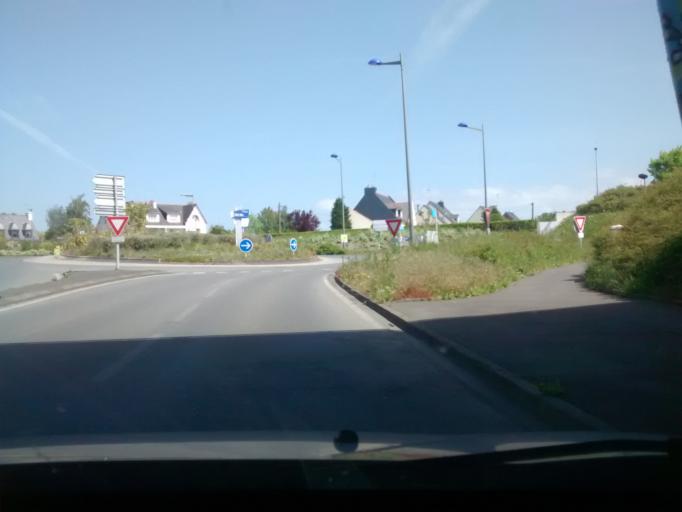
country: FR
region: Brittany
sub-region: Departement des Cotes-d'Armor
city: Langueux
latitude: 48.4966
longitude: -2.7241
